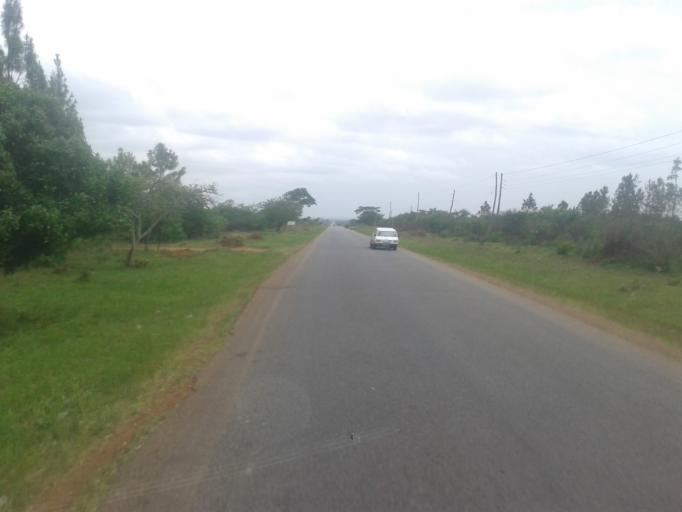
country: UG
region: Western Region
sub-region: Kiryandongo District
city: Masindi Port
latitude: 1.5103
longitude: 32.0873
